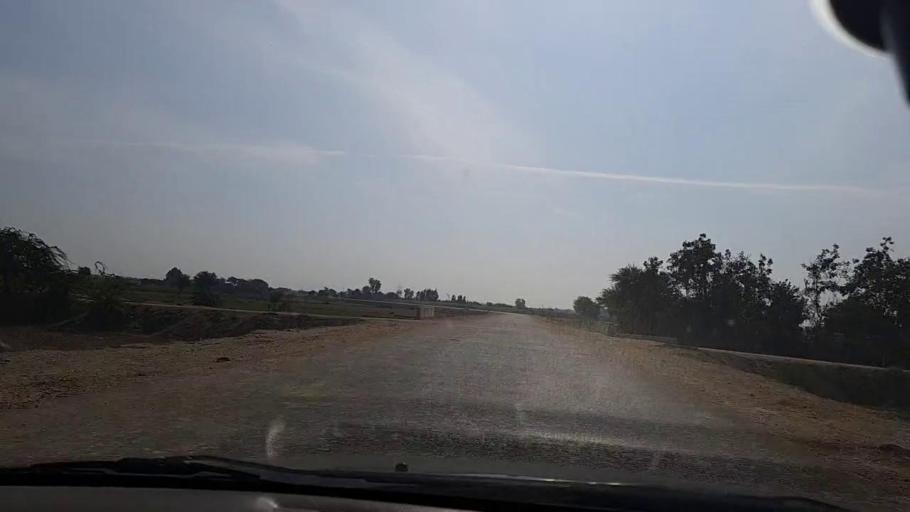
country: PK
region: Sindh
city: Mirpur Batoro
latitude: 24.7357
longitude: 68.2743
